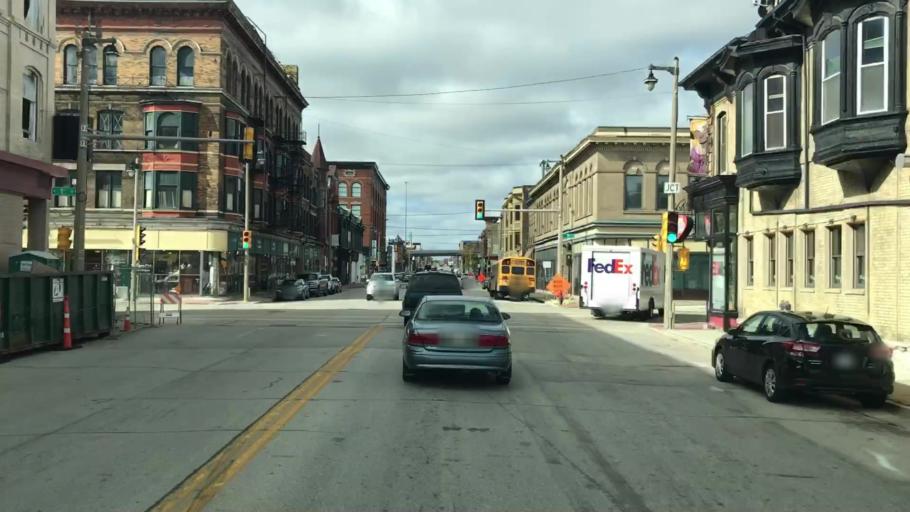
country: US
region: Wisconsin
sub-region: Milwaukee County
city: Milwaukee
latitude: 43.0233
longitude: -87.9164
